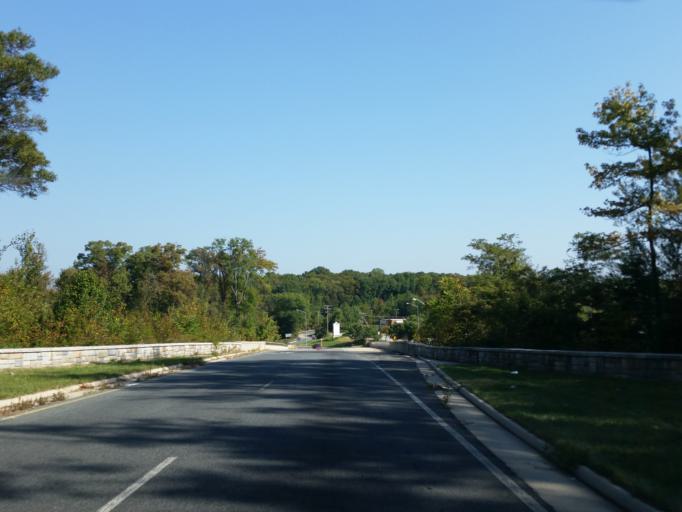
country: US
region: Maryland
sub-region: Prince George's County
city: South Laurel
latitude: 39.0543
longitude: -76.8392
